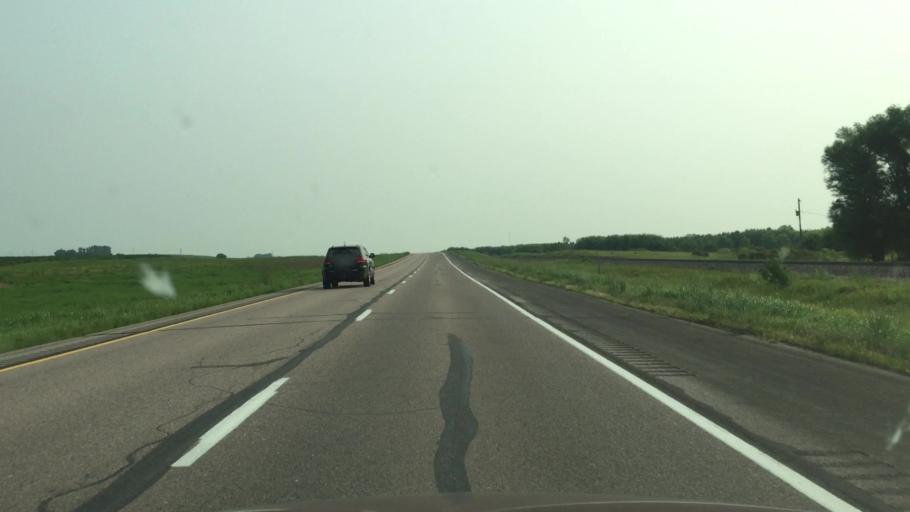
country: US
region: Iowa
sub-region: Plymouth County
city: Le Mars
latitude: 42.8816
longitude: -96.0993
